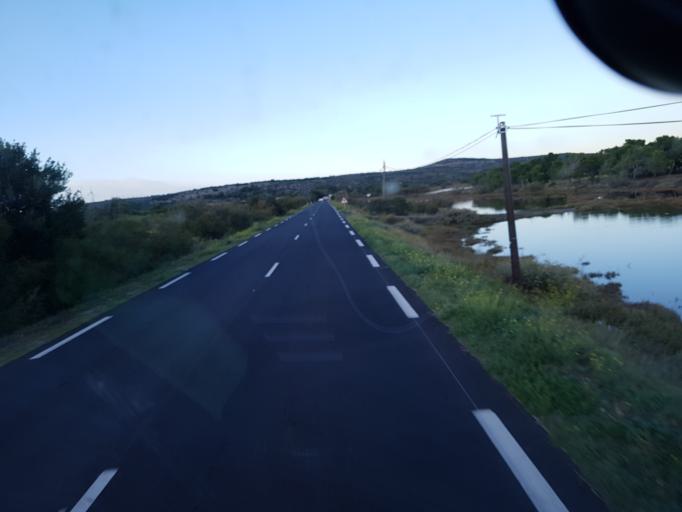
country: FR
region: Languedoc-Roussillon
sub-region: Departement de l'Aude
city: Sigean
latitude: 42.9678
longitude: 2.9982
